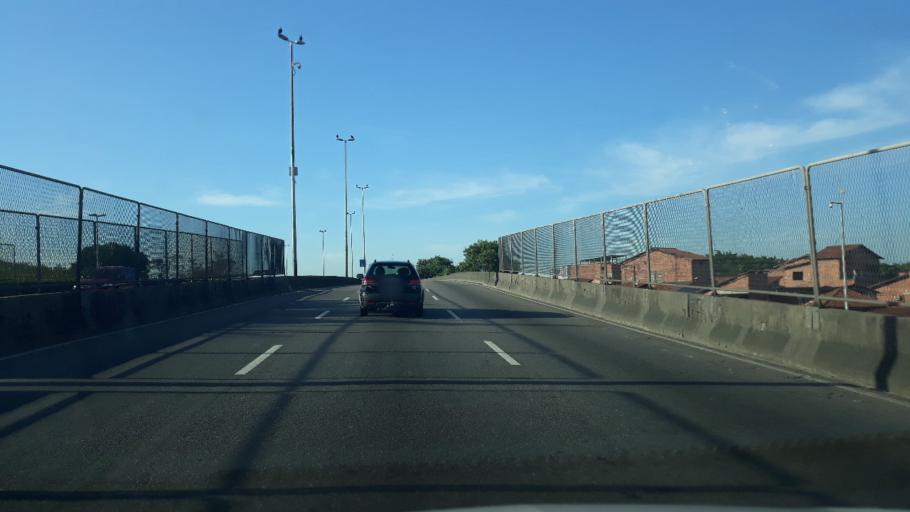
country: BR
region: Rio de Janeiro
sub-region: Sao Joao De Meriti
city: Sao Joao de Meriti
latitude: -22.9528
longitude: -43.3572
